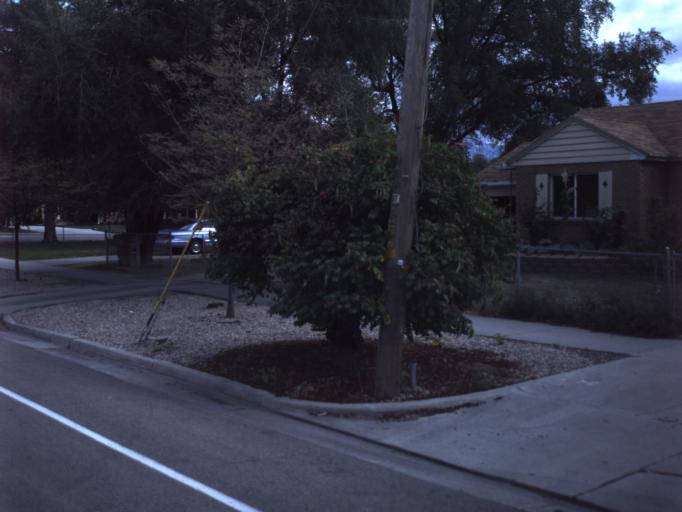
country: US
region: Utah
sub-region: Salt Lake County
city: Salt Lake City
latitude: 40.7823
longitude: -111.9148
